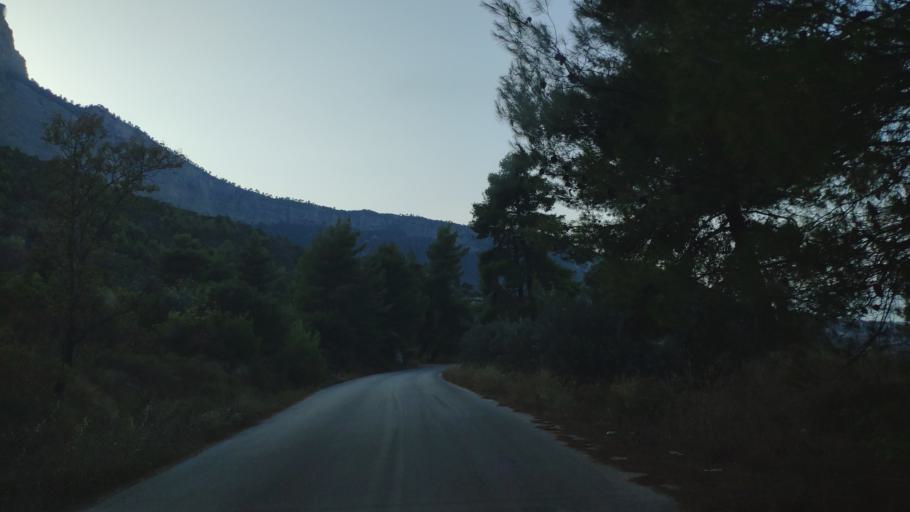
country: GR
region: West Greece
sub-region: Nomos Achaias
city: Aiyira
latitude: 38.0994
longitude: 22.3989
